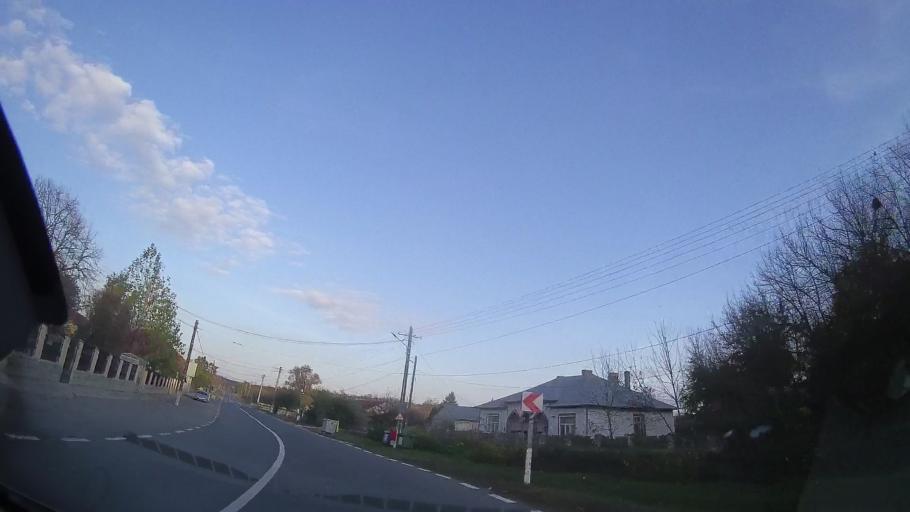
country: RO
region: Constanta
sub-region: Comuna Chirnogeni
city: Plopeni
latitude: 43.9512
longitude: 28.1953
